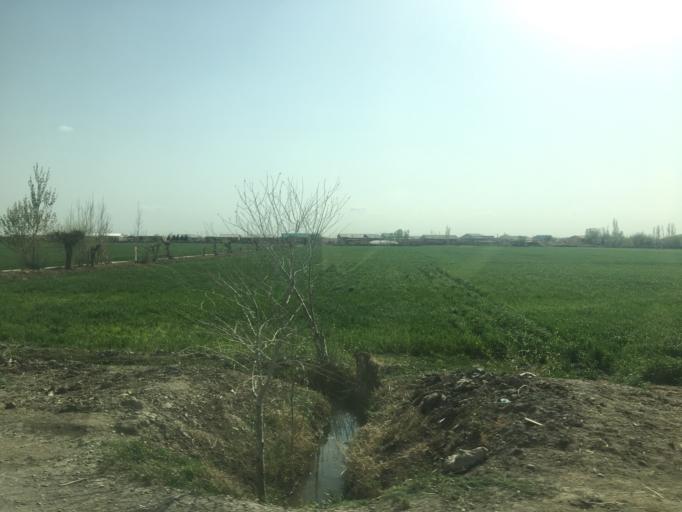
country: TM
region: Lebap
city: Farap
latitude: 39.2051
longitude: 63.5584
